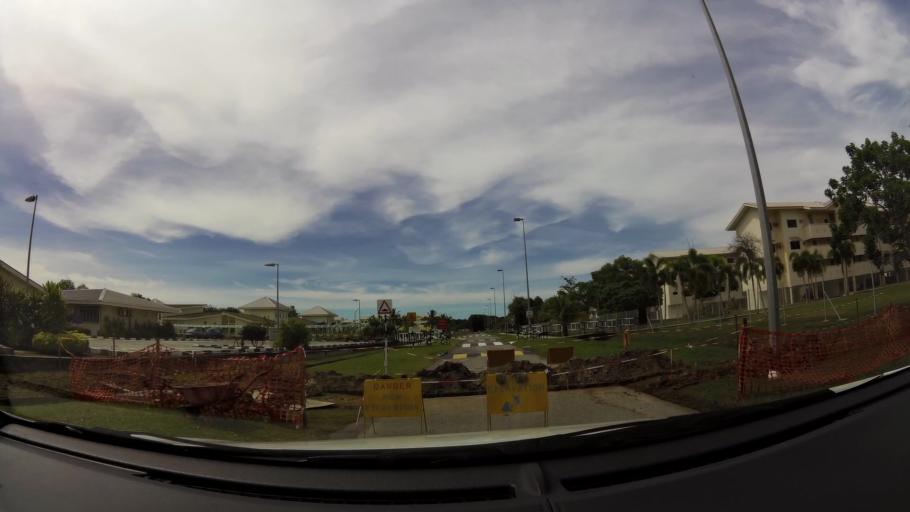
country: BN
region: Belait
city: Seria
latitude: 4.6052
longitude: 114.3130
